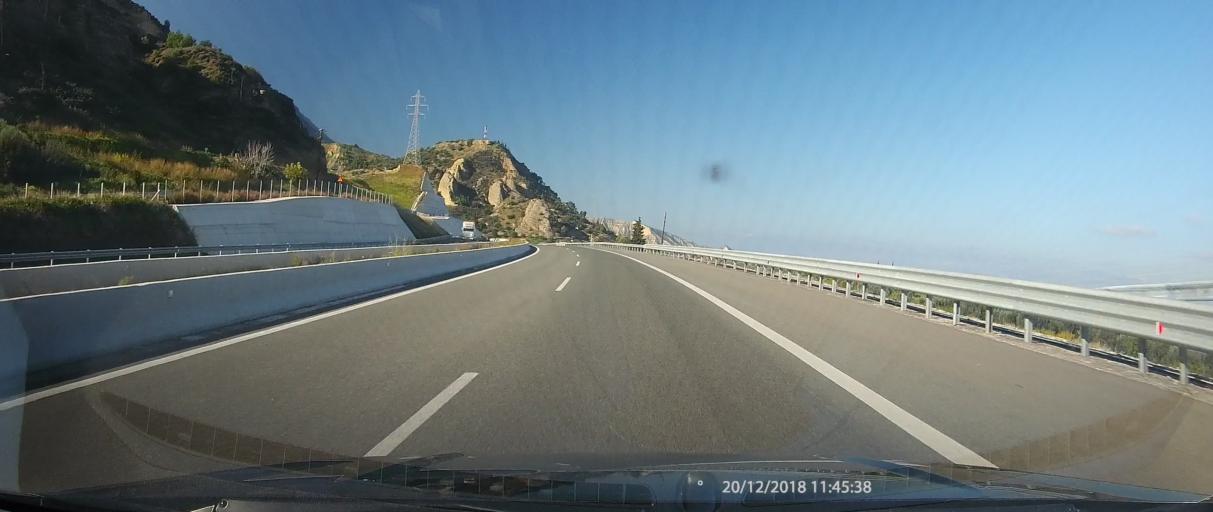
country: GR
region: Peloponnese
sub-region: Nomos Korinthias
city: Xylokastro
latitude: 38.0938
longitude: 22.5693
